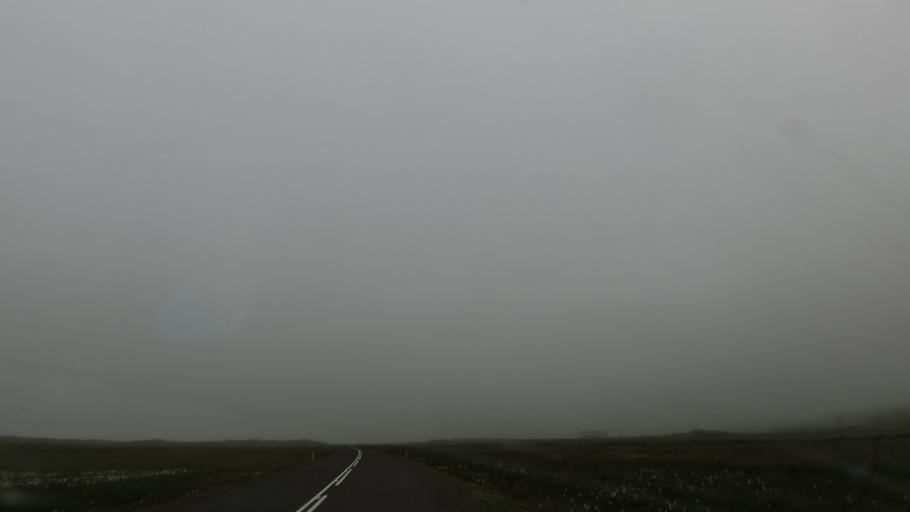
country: IS
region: East
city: Reydarfjoerdur
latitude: 64.6874
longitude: -14.3657
